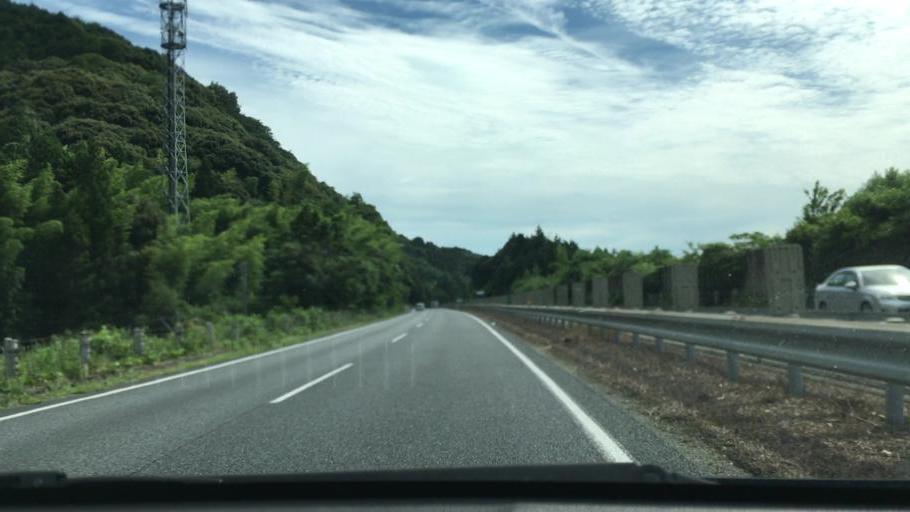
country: JP
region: Yamaguchi
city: Ogori-shimogo
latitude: 34.1283
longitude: 131.4220
